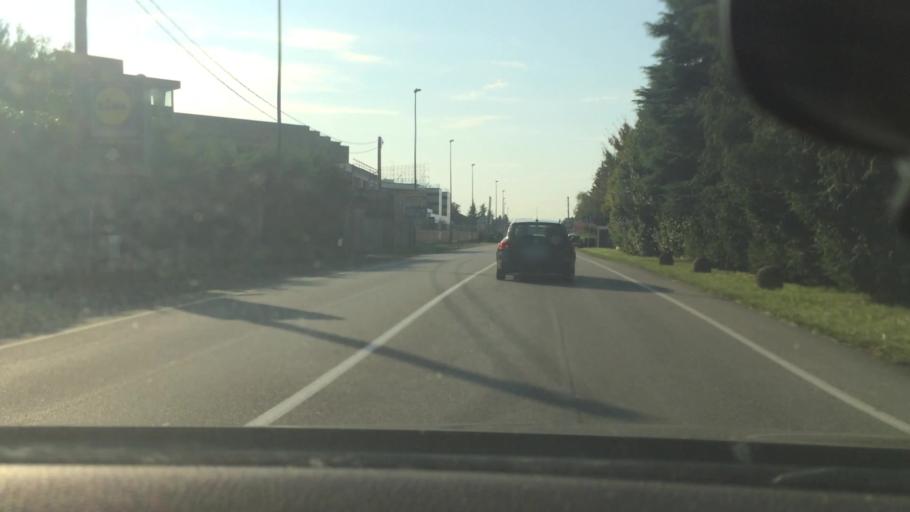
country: IT
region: Lombardy
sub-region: Provincia di Varese
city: Gerenzano
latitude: 45.6370
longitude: 9.0095
